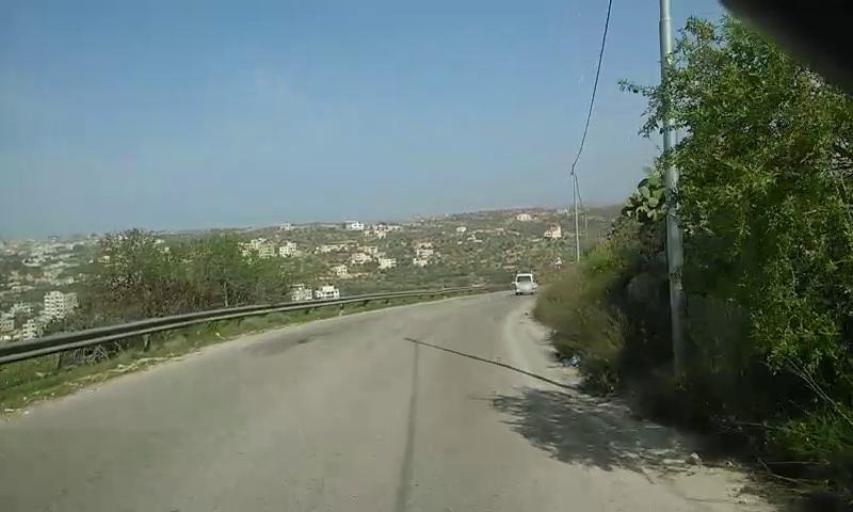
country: PS
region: West Bank
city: Dura al Qar`
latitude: 31.9598
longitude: 35.2245
